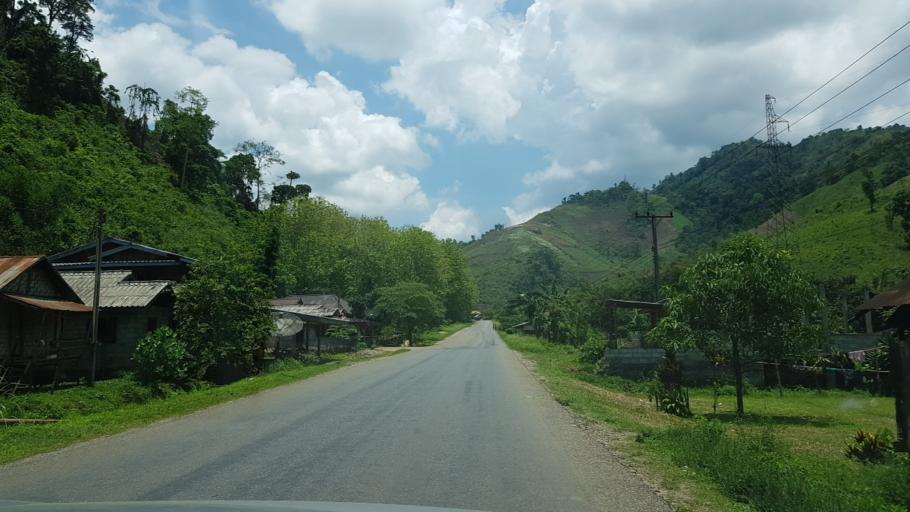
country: LA
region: Vientiane
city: Muang Kasi
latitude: 19.1323
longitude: 102.2808
